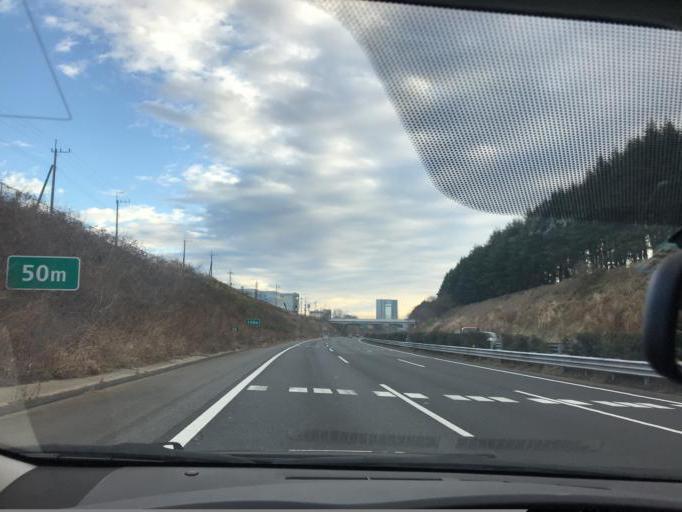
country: JP
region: Ibaraki
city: Naka
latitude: 36.0351
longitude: 140.0939
